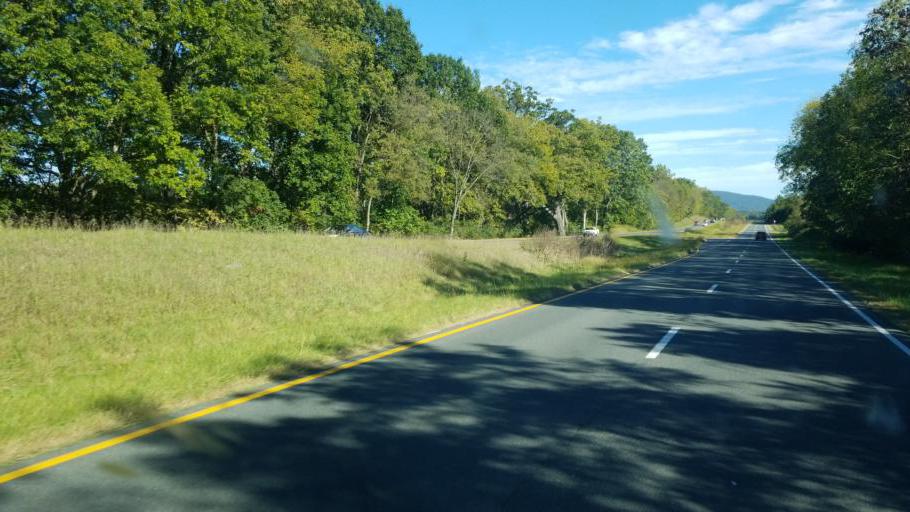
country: US
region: Virginia
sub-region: Warren County
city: Shenandoah Farms
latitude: 39.0644
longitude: -78.0519
